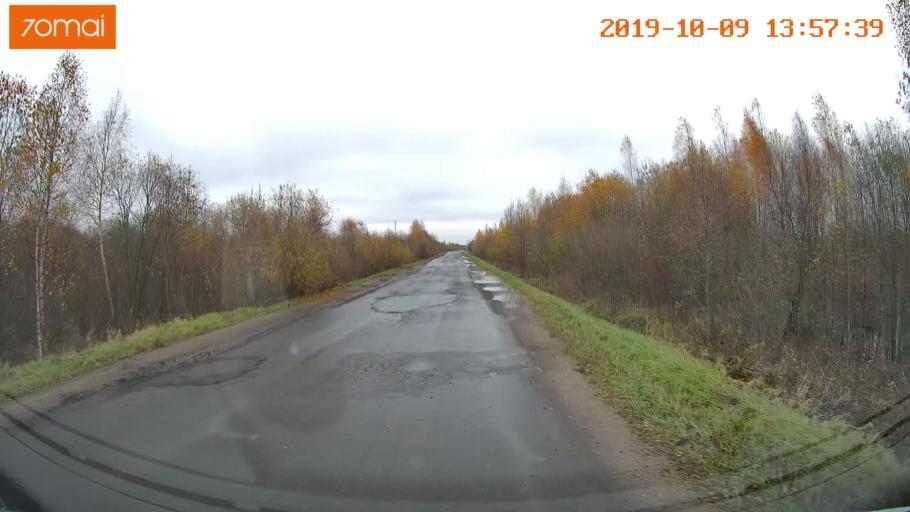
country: RU
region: Kostroma
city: Buy
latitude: 58.4316
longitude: 41.2983
